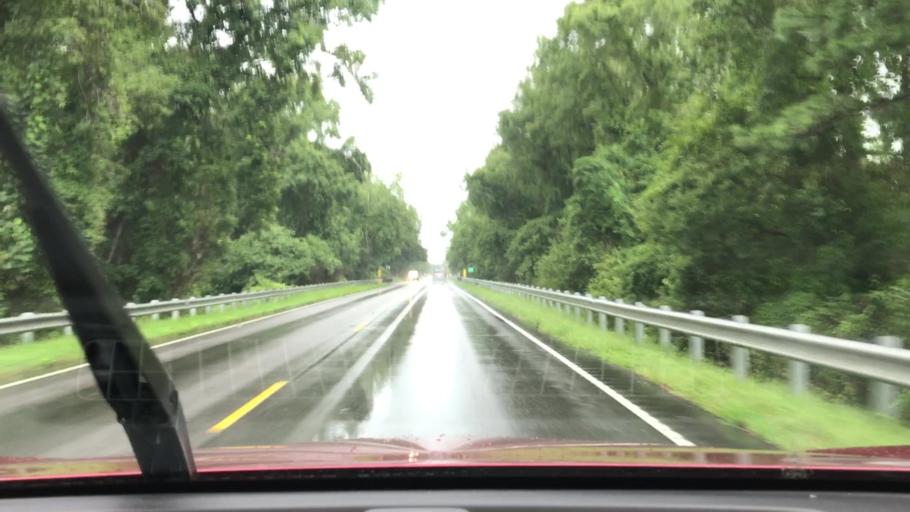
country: US
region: South Carolina
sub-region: Horry County
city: Socastee
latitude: 33.6860
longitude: -79.1222
